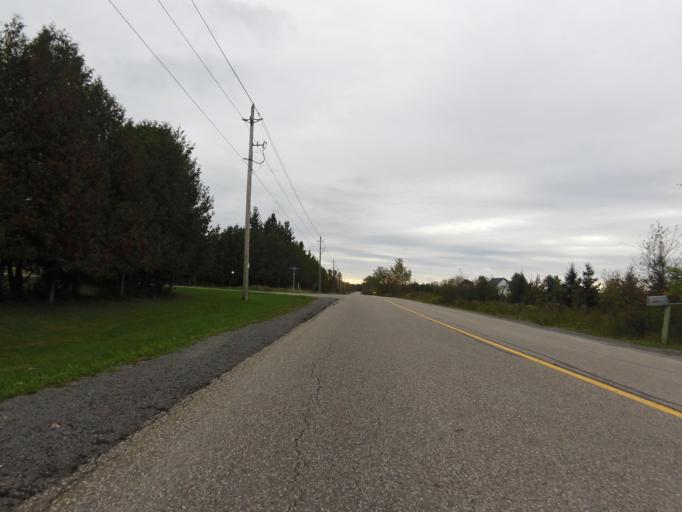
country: CA
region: Ontario
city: Bells Corners
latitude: 45.4032
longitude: -76.0699
